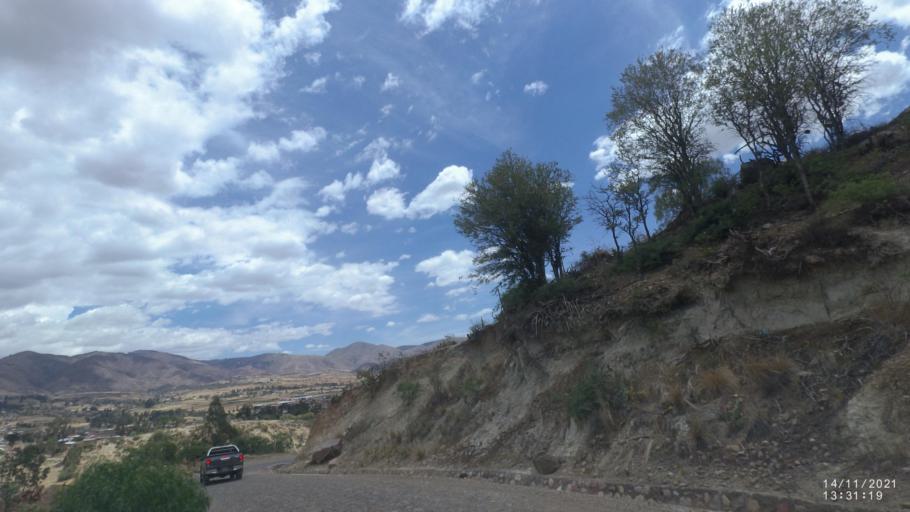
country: BO
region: Cochabamba
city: Colomi
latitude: -17.3950
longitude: -65.9812
